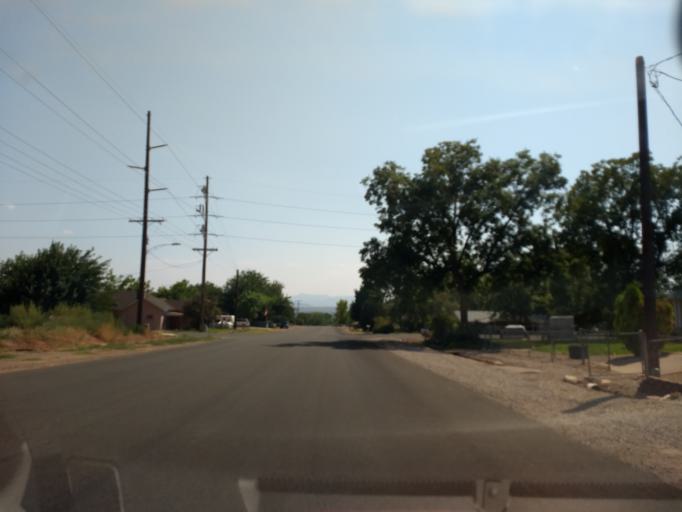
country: US
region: Utah
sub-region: Washington County
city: Washington
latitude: 37.1283
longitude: -113.5099
